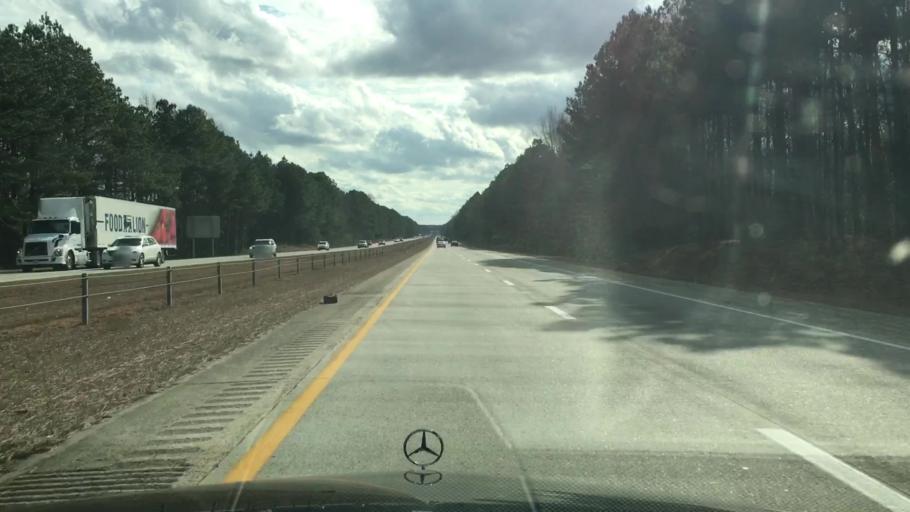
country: US
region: North Carolina
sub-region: Johnston County
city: Benson
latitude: 35.5068
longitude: -78.5553
